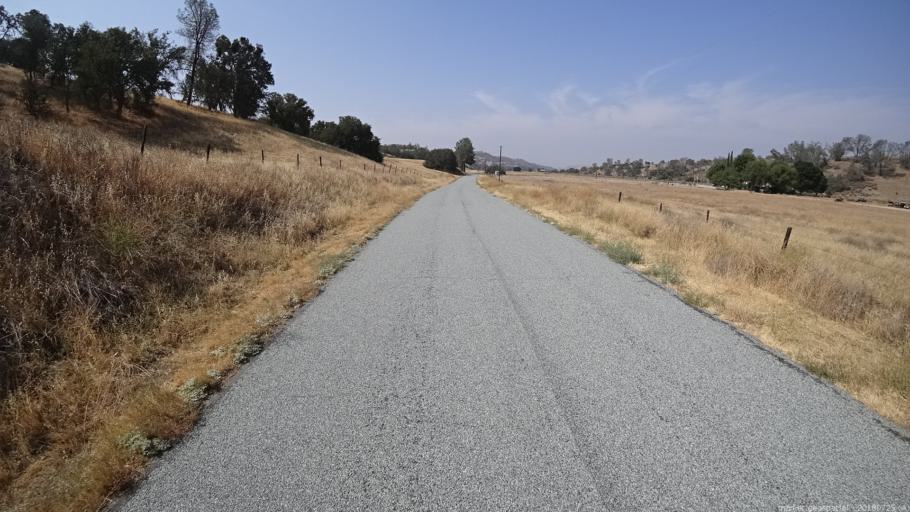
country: US
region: California
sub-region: San Luis Obispo County
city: San Miguel
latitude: 35.8512
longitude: -120.6085
